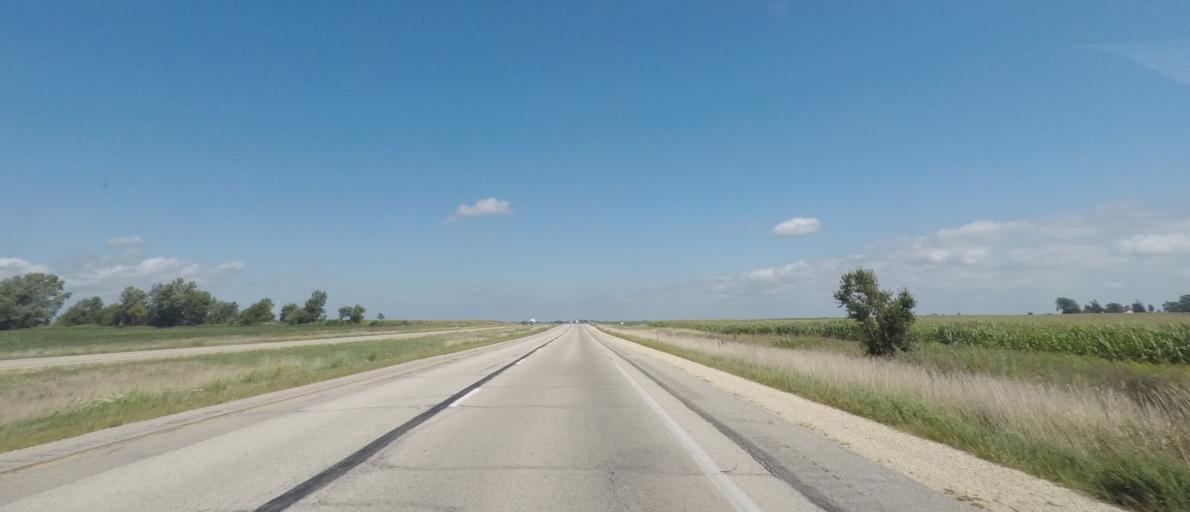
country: US
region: Iowa
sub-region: Linn County
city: Springville
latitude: 42.0681
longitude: -91.3772
